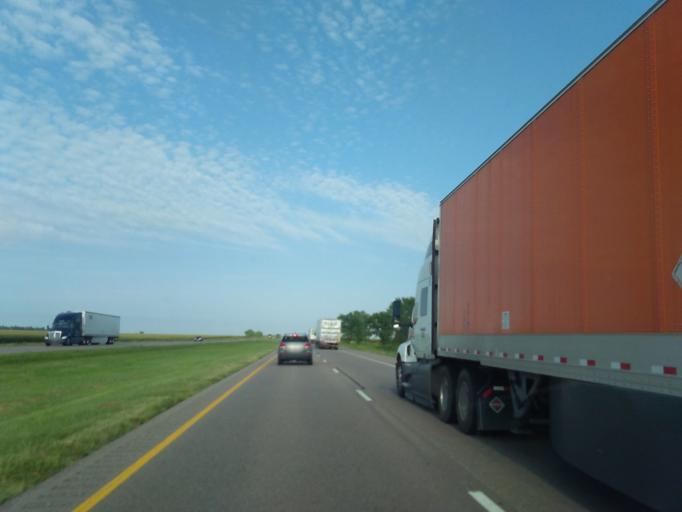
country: US
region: Nebraska
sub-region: York County
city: York
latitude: 40.8216
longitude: -97.7336
